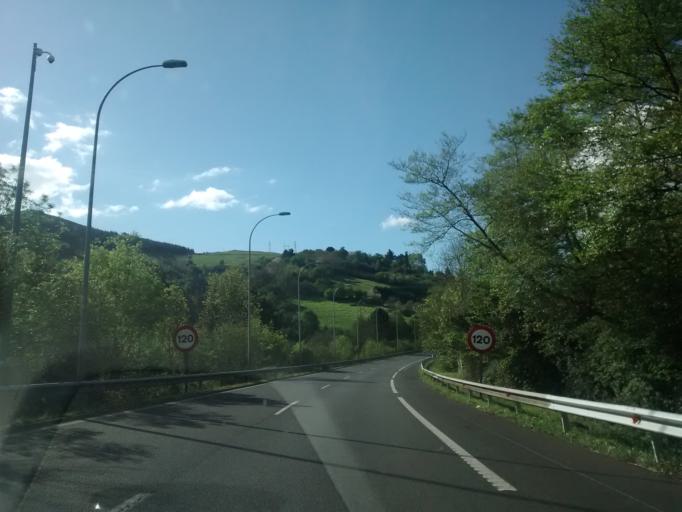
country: ES
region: Basque Country
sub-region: Bizkaia
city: Santutxu
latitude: 43.2333
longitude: -2.9159
